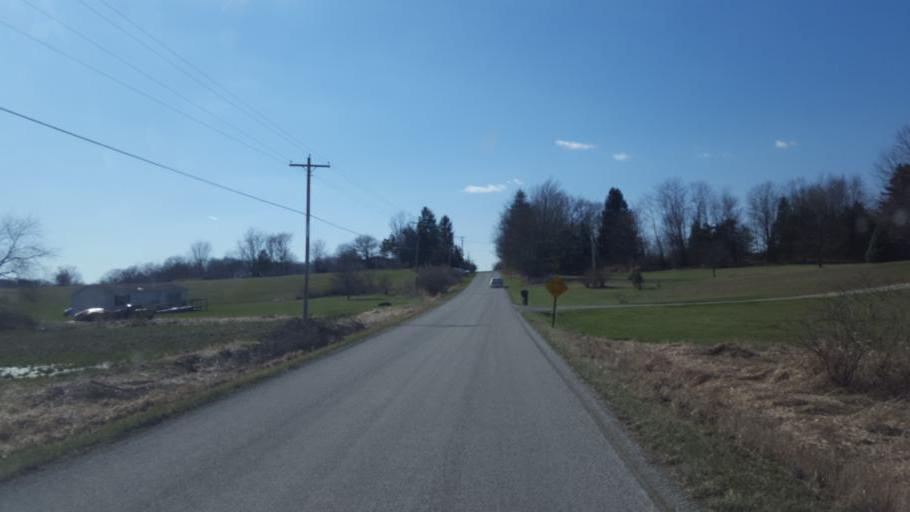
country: US
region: Ohio
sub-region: Morrow County
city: Mount Gilead
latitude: 40.4586
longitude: -82.7262
